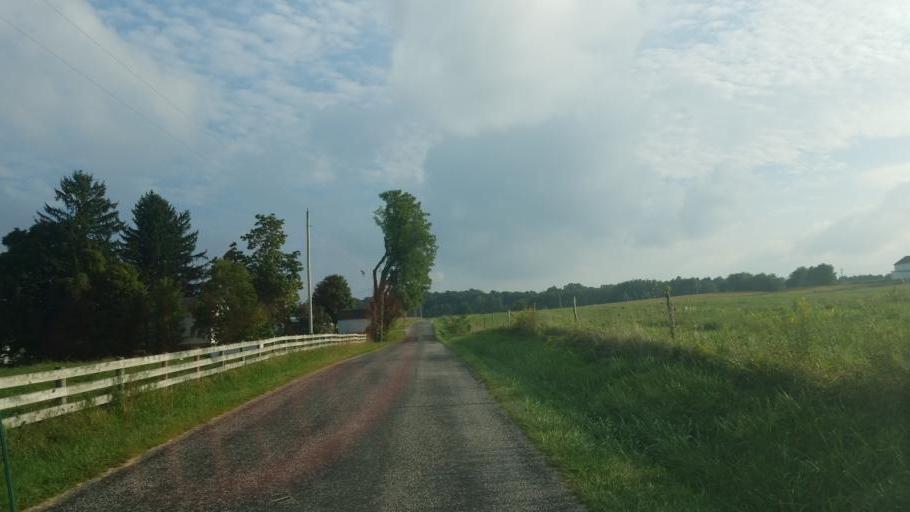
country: US
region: Ohio
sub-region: Wayne County
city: Wooster
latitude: 40.8610
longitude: -82.0293
